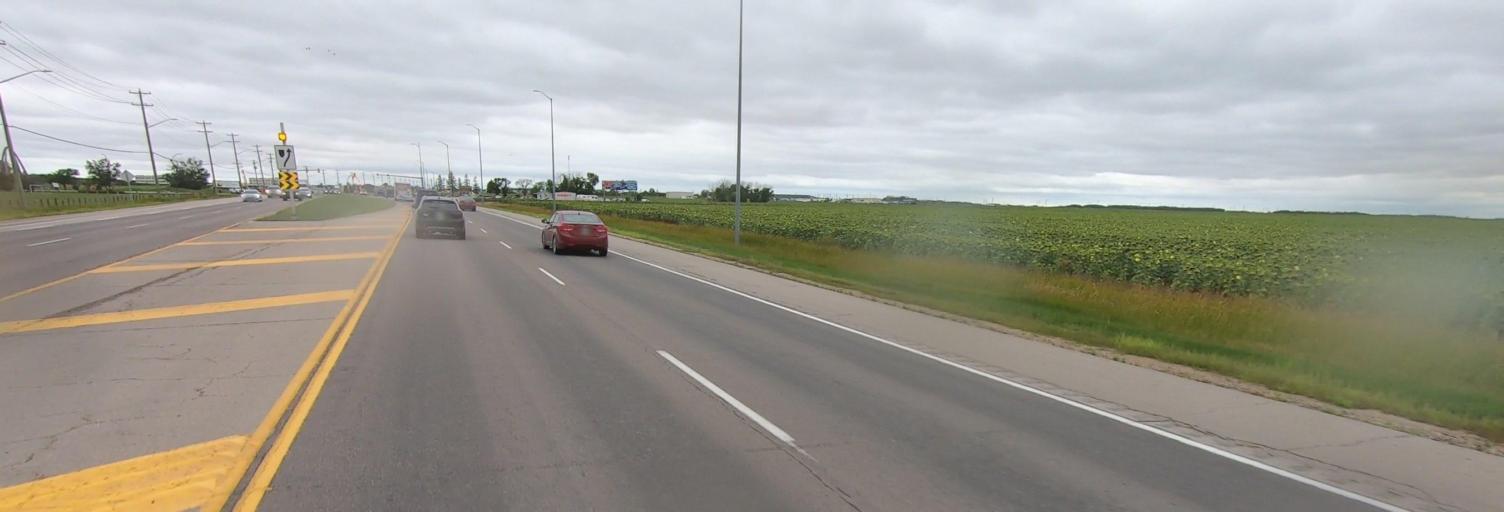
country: CA
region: Manitoba
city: Headingley
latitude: 49.8768
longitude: -97.3572
